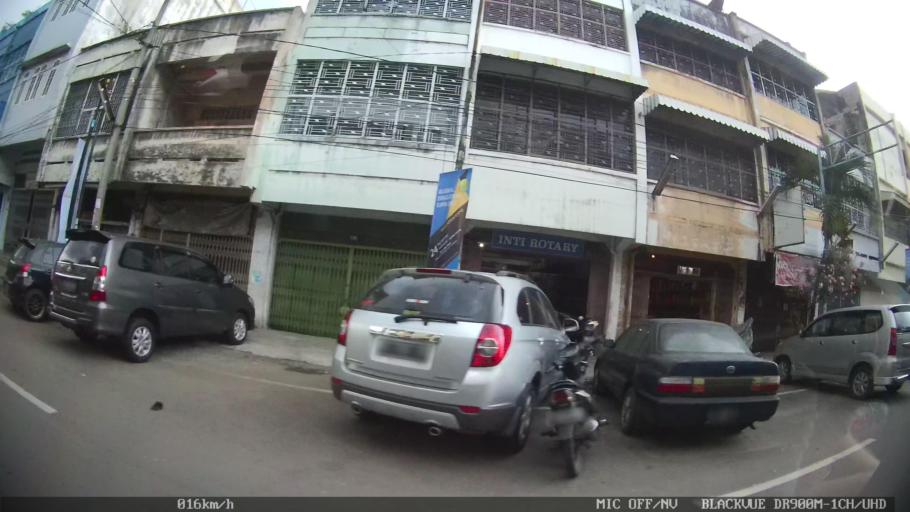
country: ID
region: North Sumatra
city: Medan
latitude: 3.5805
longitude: 98.6886
